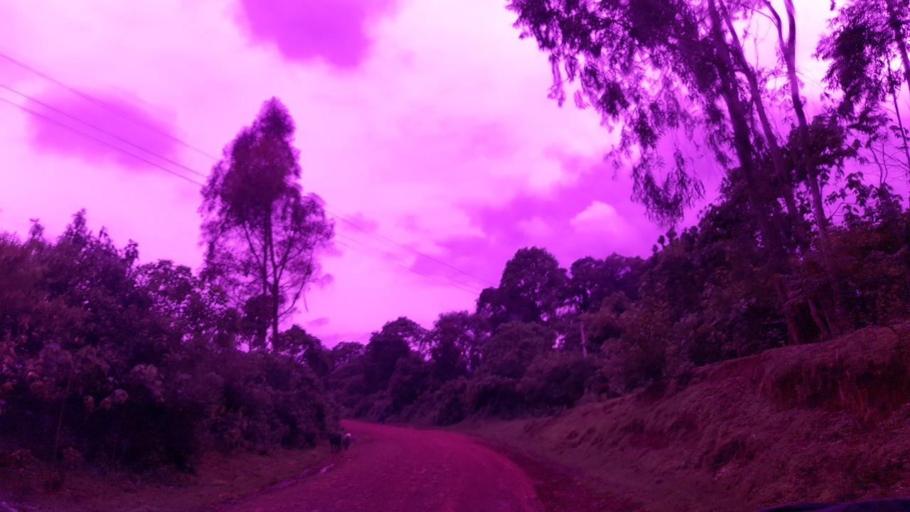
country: ET
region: Southern Nations, Nationalities, and People's Region
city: Tippi
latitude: 7.5736
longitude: 35.6419
